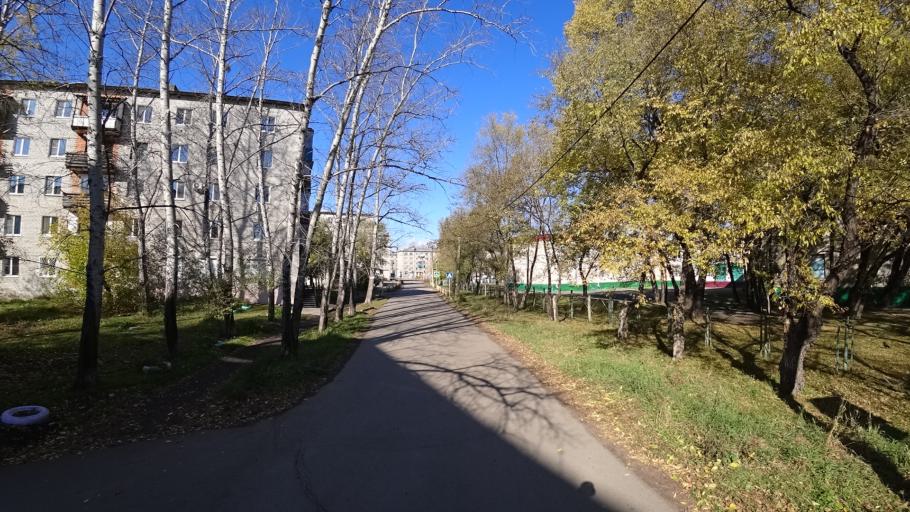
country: RU
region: Khabarovsk Krai
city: Amursk
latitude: 50.0978
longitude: 136.5144
